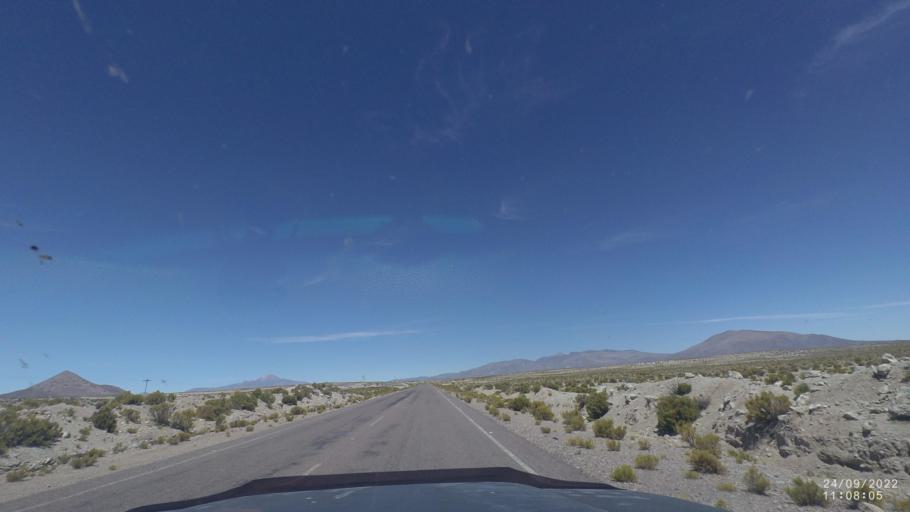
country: BO
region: Oruro
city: Challapata
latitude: -19.4819
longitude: -67.4380
